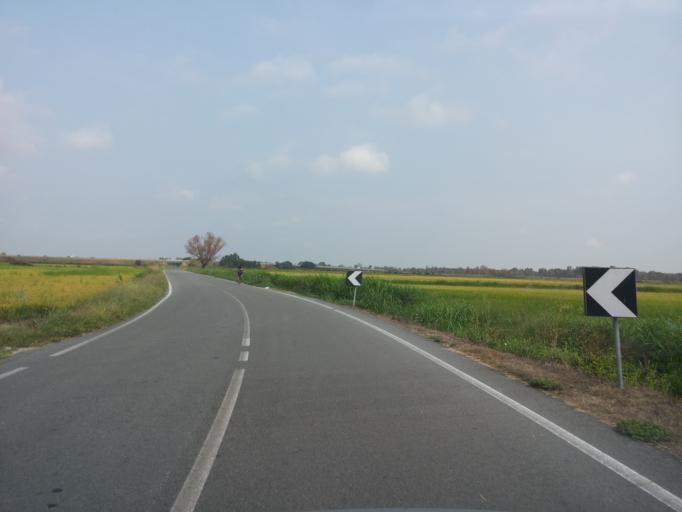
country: IT
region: Piedmont
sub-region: Provincia di Vercelli
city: Prarolo
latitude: 45.2878
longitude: 8.4763
